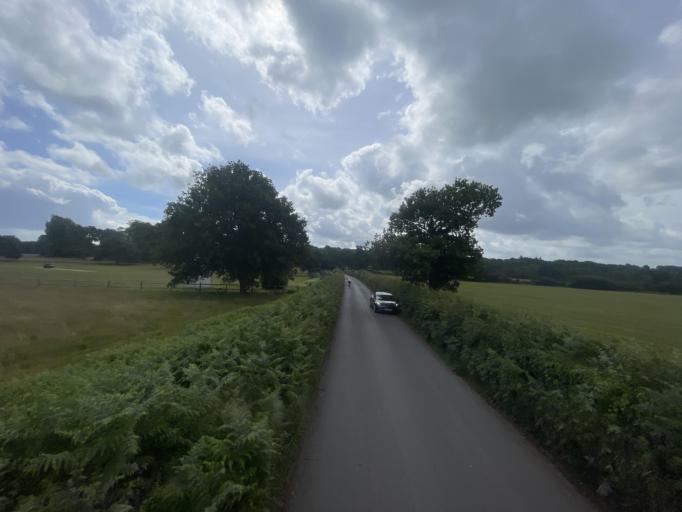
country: GB
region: England
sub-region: Kent
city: Edenbridge
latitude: 51.1589
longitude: 0.1481
